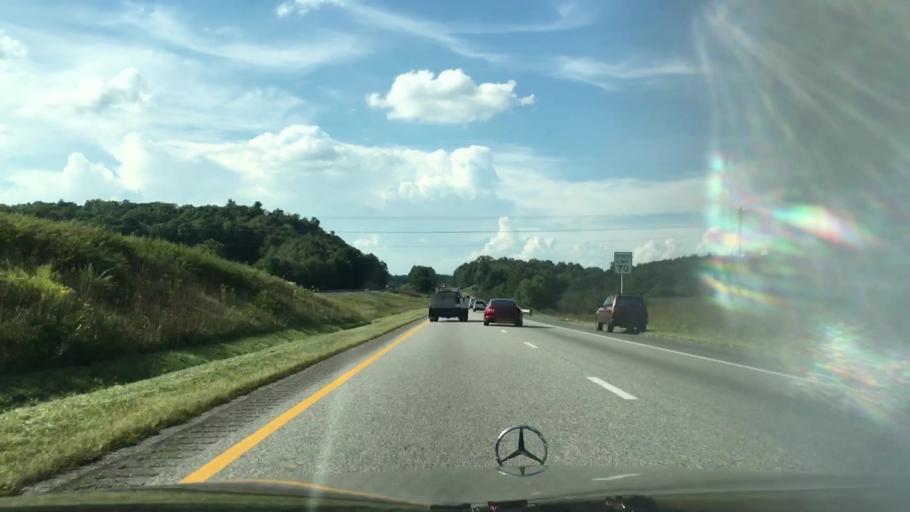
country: US
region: Virginia
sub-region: Augusta County
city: Fishersville
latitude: 38.0916
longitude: -78.9971
